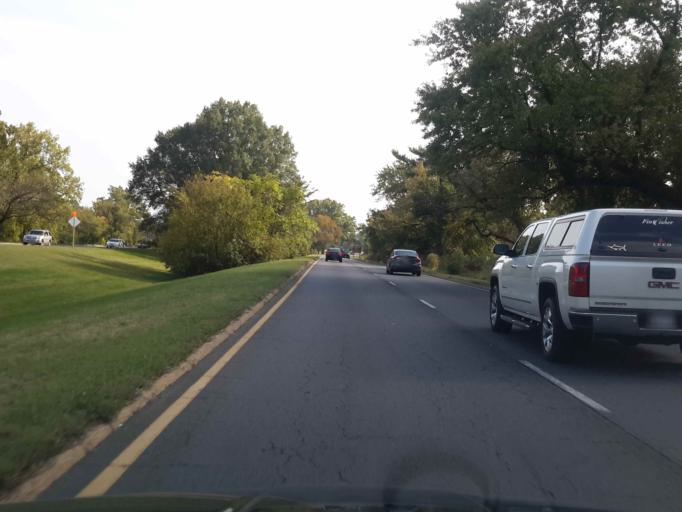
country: US
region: Virginia
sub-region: City of Alexandria
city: Alexandria
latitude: 38.8340
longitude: -77.0455
